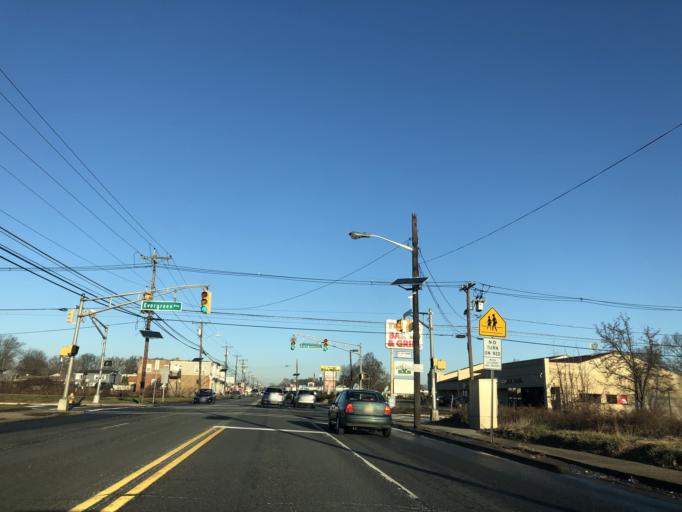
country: US
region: New Jersey
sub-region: Camden County
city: Somerdale
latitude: 39.8505
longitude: -75.0234
